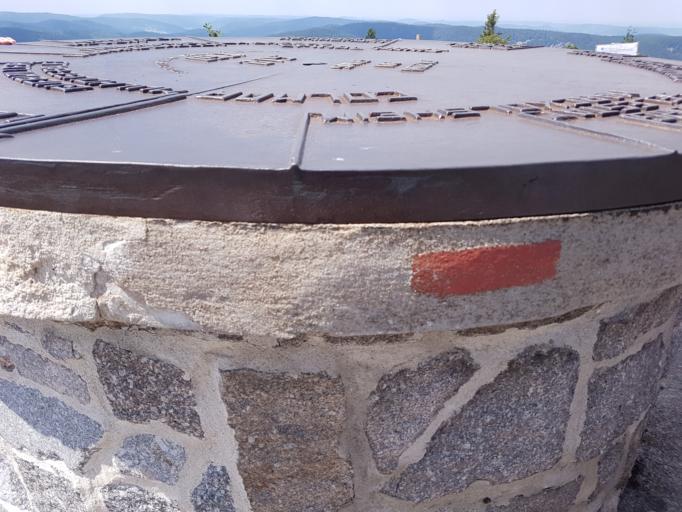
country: FR
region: Alsace
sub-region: Departement du Haut-Rhin
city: Soultzeren
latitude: 48.1066
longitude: 7.0704
